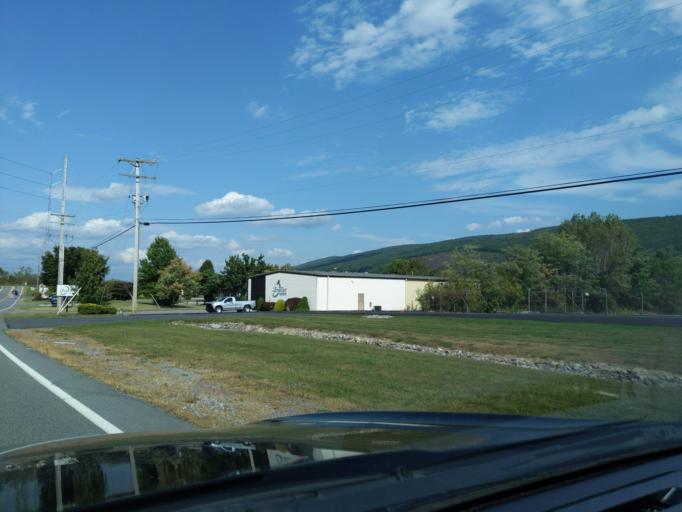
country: US
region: Pennsylvania
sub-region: Blair County
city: Lakemont
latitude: 40.4824
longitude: -78.3960
